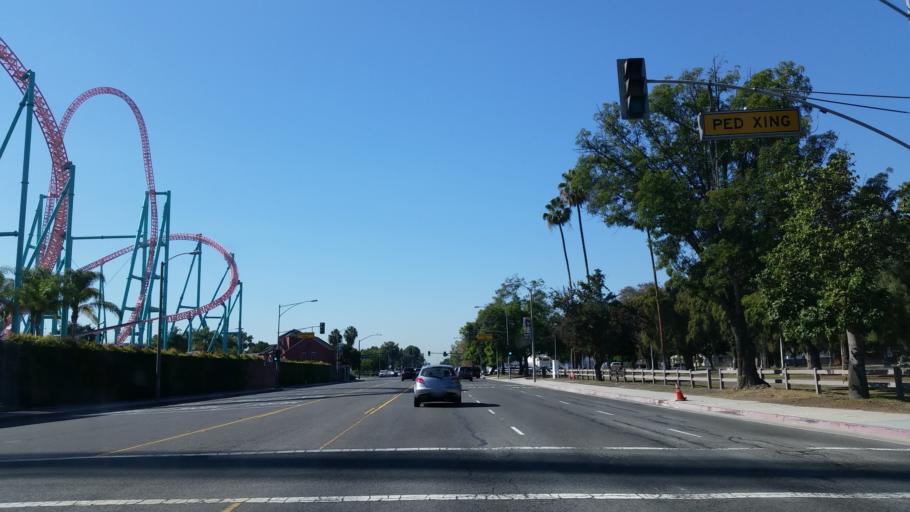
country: US
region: California
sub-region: Orange County
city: Buena Park
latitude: 33.8467
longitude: -118.0002
